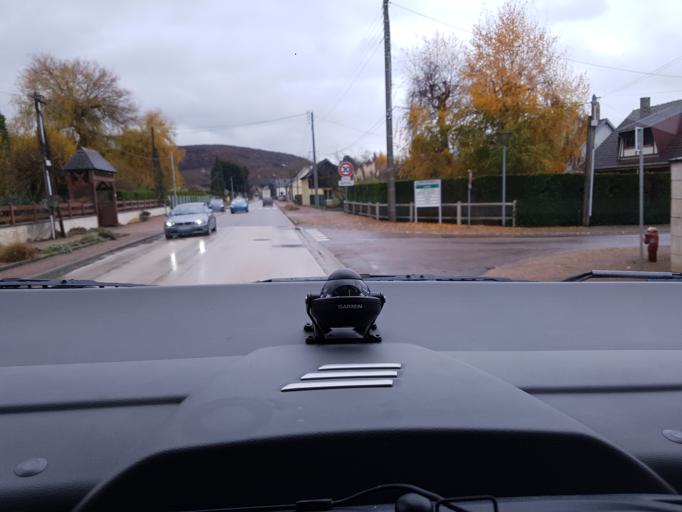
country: FR
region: Haute-Normandie
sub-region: Departement de l'Eure
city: Romilly-sur-Andelle
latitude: 49.3326
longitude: 1.2504
